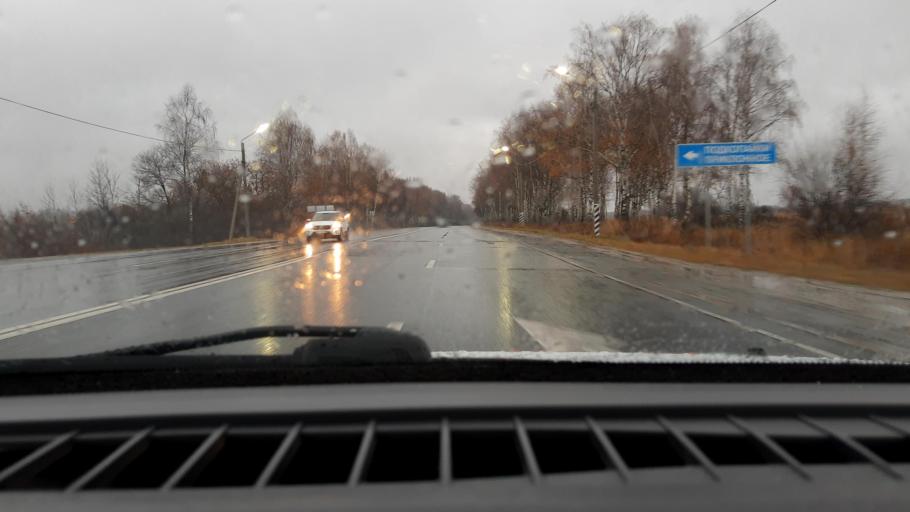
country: RU
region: Nizjnij Novgorod
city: Sitniki
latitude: 56.5075
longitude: 44.0234
